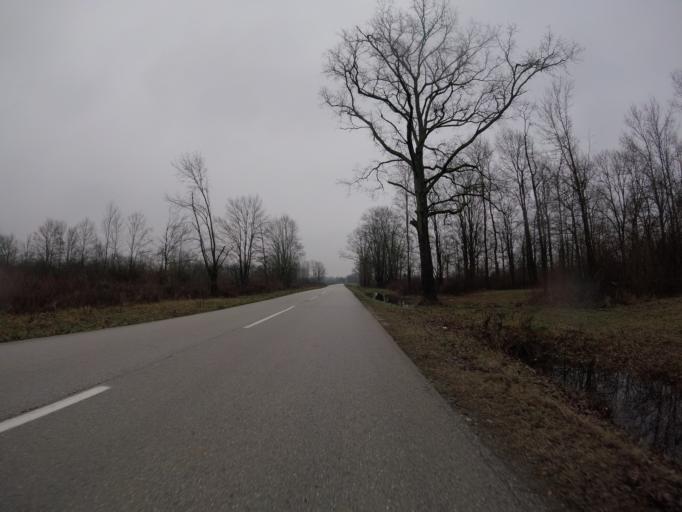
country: HR
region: Zagrebacka
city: Kuce
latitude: 45.7045
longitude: 16.1971
